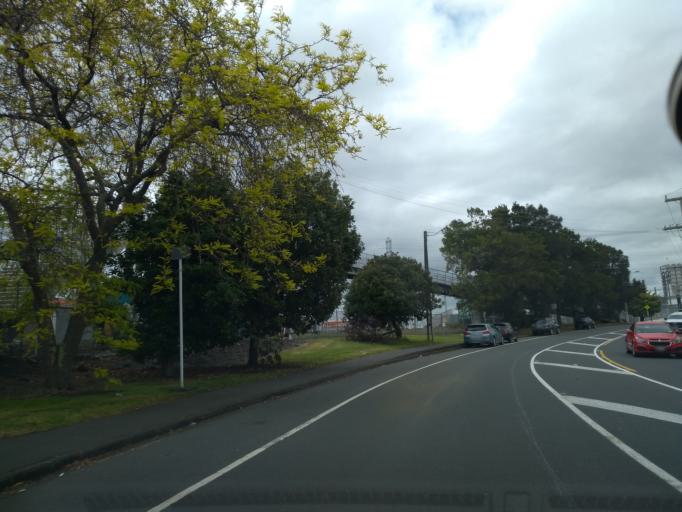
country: NZ
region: Auckland
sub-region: Auckland
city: Tamaki
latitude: -36.9099
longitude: 174.8150
